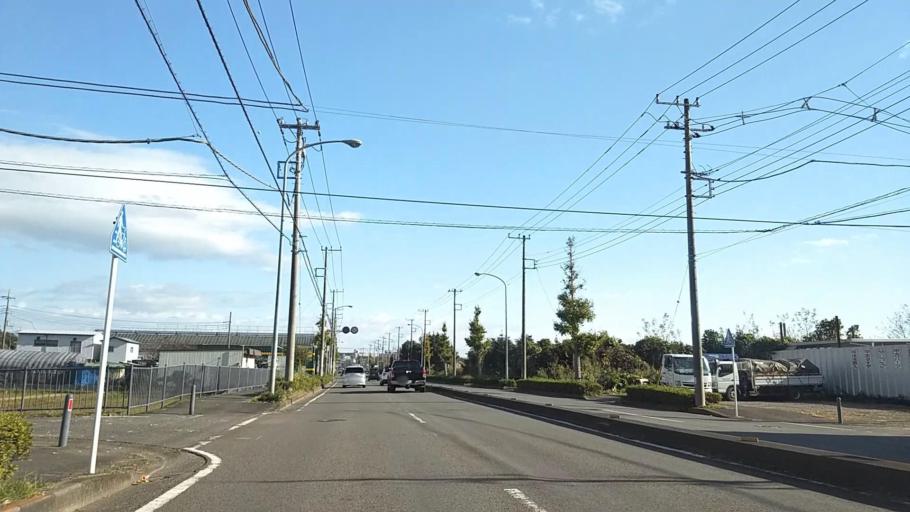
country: JP
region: Tokyo
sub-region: Machida-shi
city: Machida
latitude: 35.5612
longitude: 139.5210
